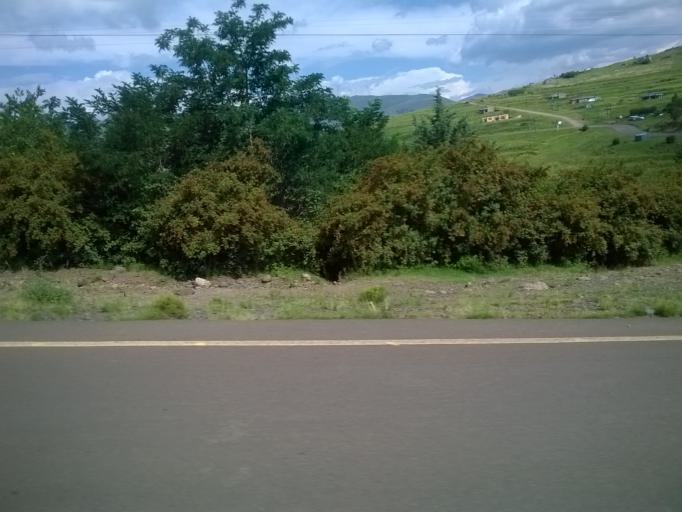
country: LS
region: Thaba-Tseka
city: Thaba-Tseka
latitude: -29.1414
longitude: 28.4882
